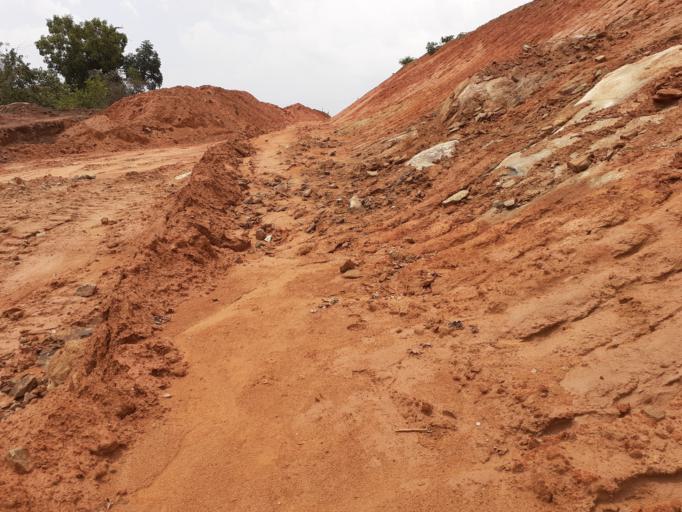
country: ET
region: Oromiya
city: Gimbi
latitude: 9.3336
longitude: 35.6956
